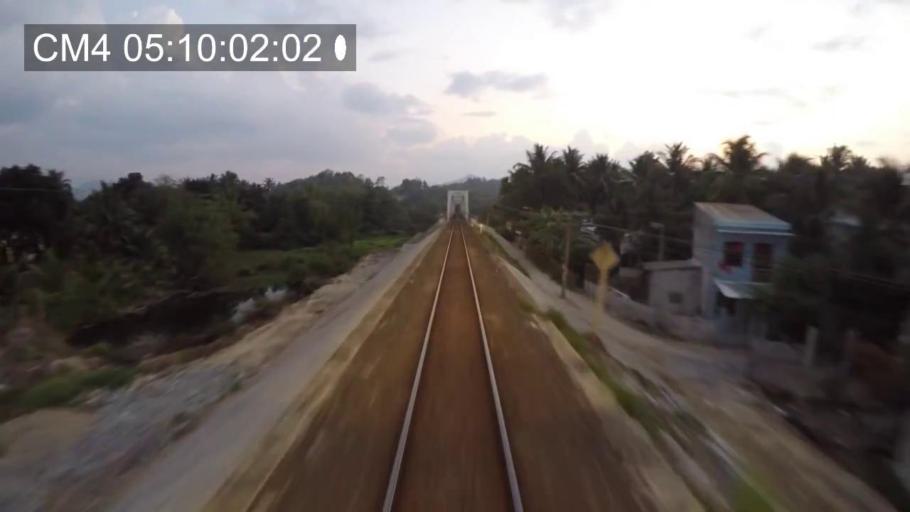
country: VN
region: Khanh Hoa
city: Nha Trang
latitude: 12.3057
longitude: 109.1862
